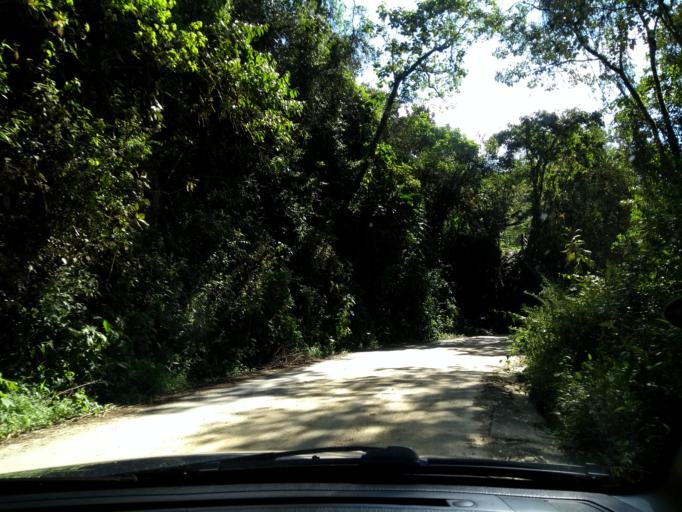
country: CO
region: Caldas
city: Salamina
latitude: 5.3754
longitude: -75.4507
